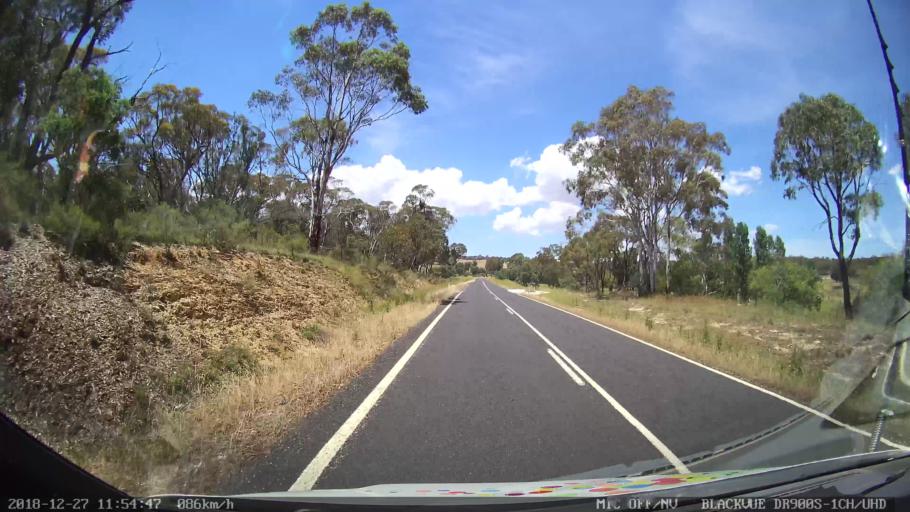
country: AU
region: New South Wales
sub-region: Blayney
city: Blayney
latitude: -33.6793
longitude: 149.4015
